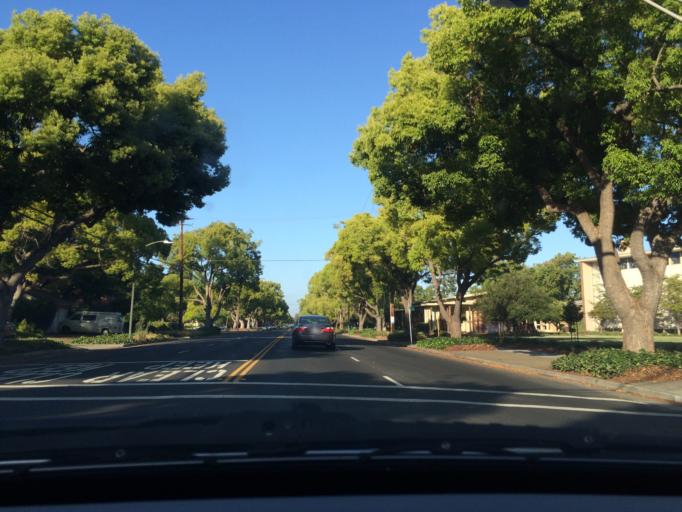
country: US
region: California
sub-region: Santa Clara County
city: Palo Alto
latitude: 37.4446
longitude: -122.1346
